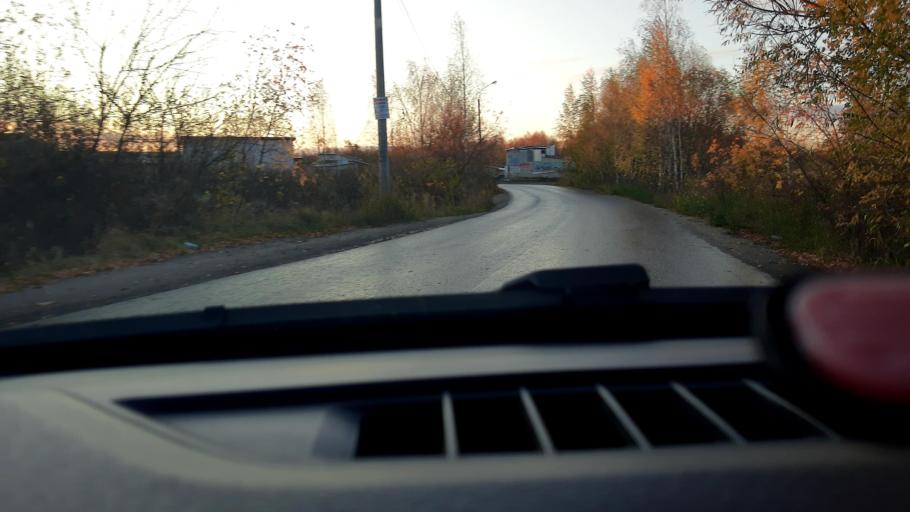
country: RU
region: Nizjnij Novgorod
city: Gorbatovka
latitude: 56.3320
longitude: 43.8139
